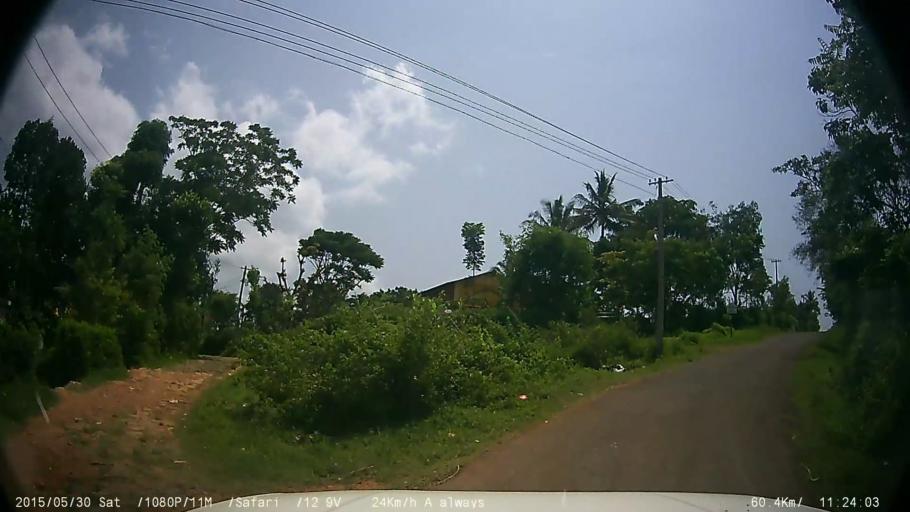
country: IN
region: Kerala
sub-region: Wayanad
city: Panamaram
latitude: 11.8042
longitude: 76.0282
